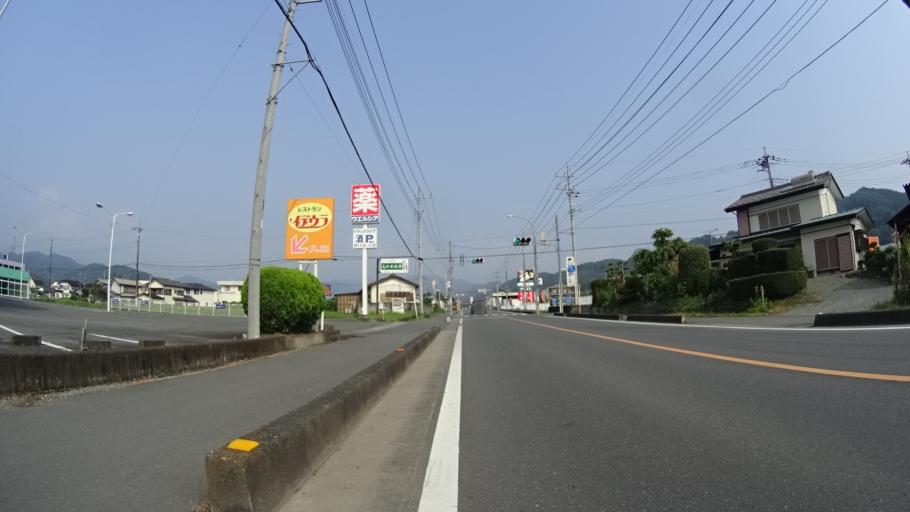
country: JP
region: Saitama
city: Chichibu
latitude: 36.0212
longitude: 139.0079
